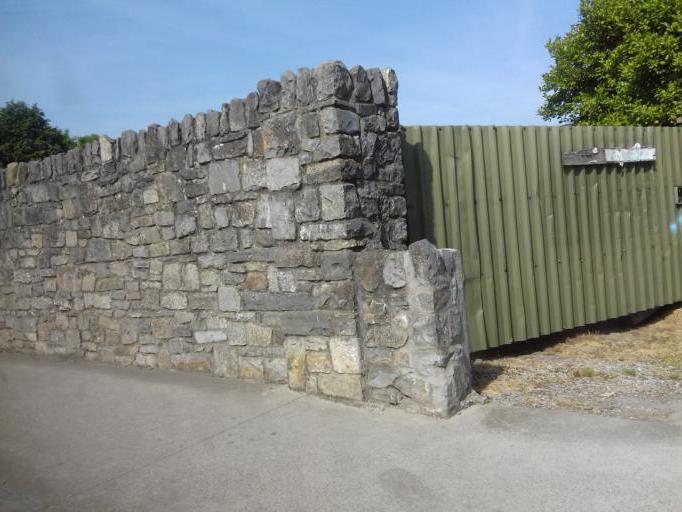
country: IE
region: Leinster
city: Lusk
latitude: 53.5258
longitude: -6.1657
